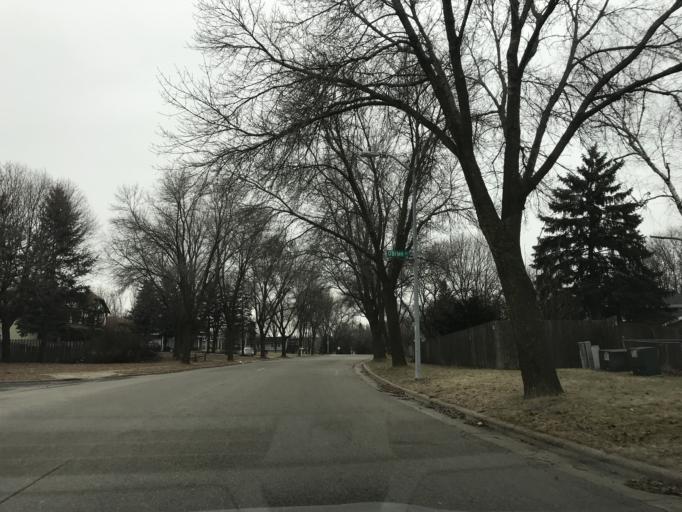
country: US
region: Wisconsin
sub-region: Dane County
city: Monona
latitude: 43.1005
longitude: -89.2889
